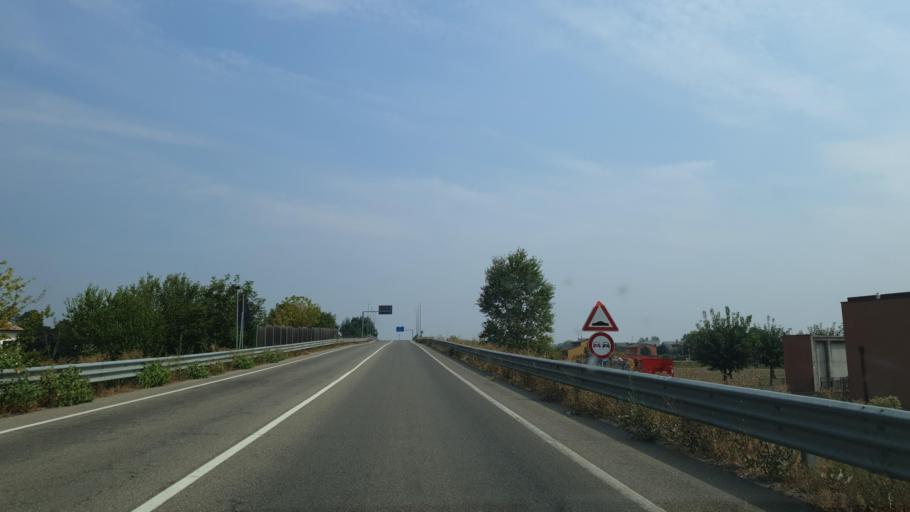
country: IT
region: Emilia-Romagna
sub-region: Provincia di Parma
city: San Secondo Parmense
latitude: 44.9285
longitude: 10.2286
